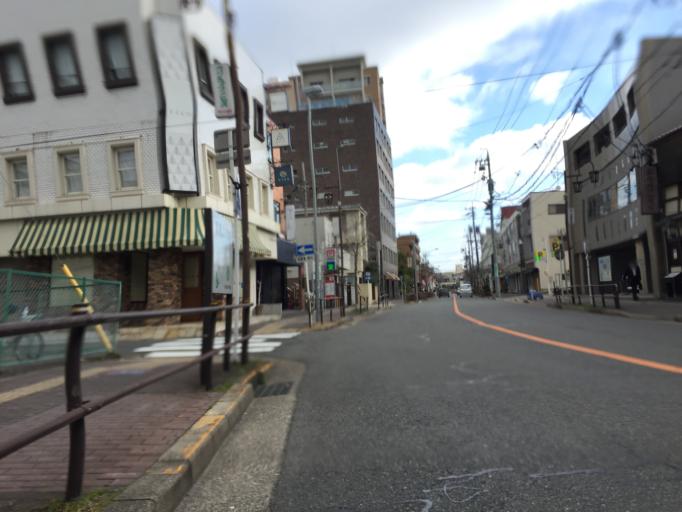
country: JP
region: Aichi
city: Nagoya-shi
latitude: 35.1691
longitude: 136.9458
